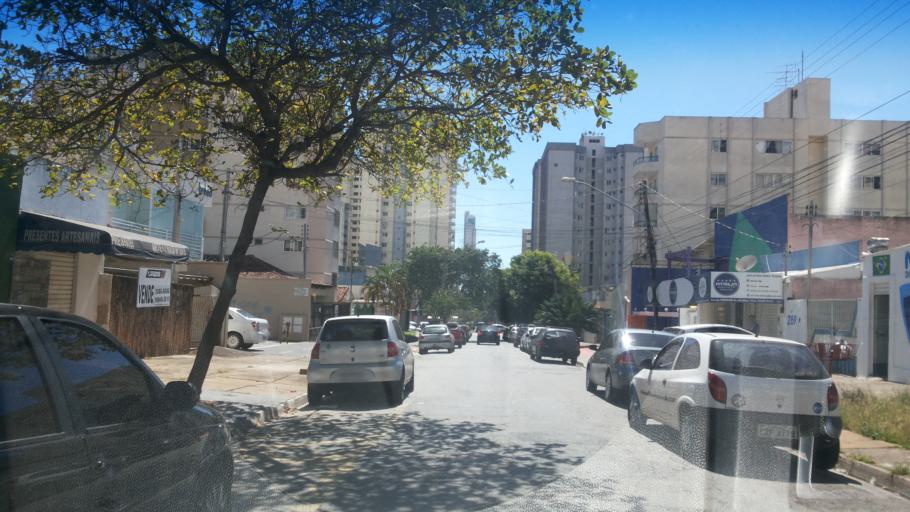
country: BR
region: Goias
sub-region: Goiania
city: Goiania
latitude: -16.7151
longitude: -49.2620
